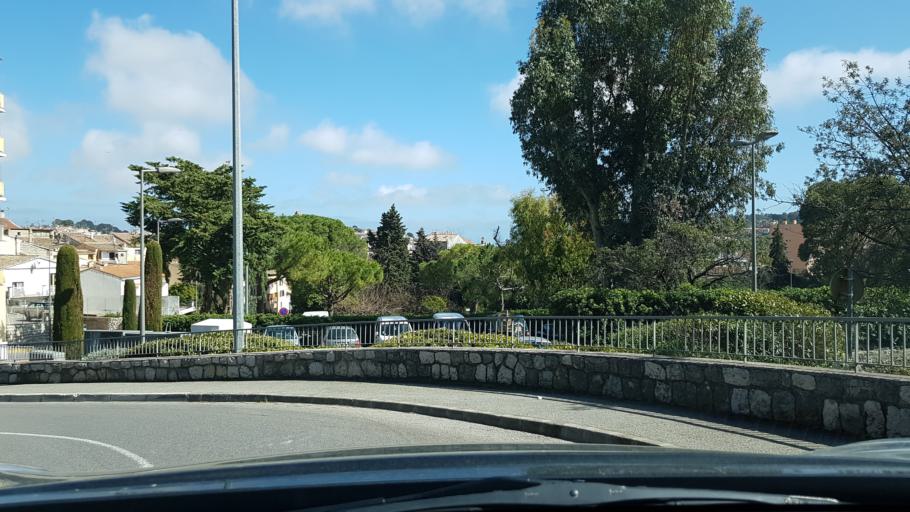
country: FR
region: Provence-Alpes-Cote d'Azur
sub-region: Departement des Alpes-Maritimes
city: Vallauris
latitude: 43.5792
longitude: 7.0490
